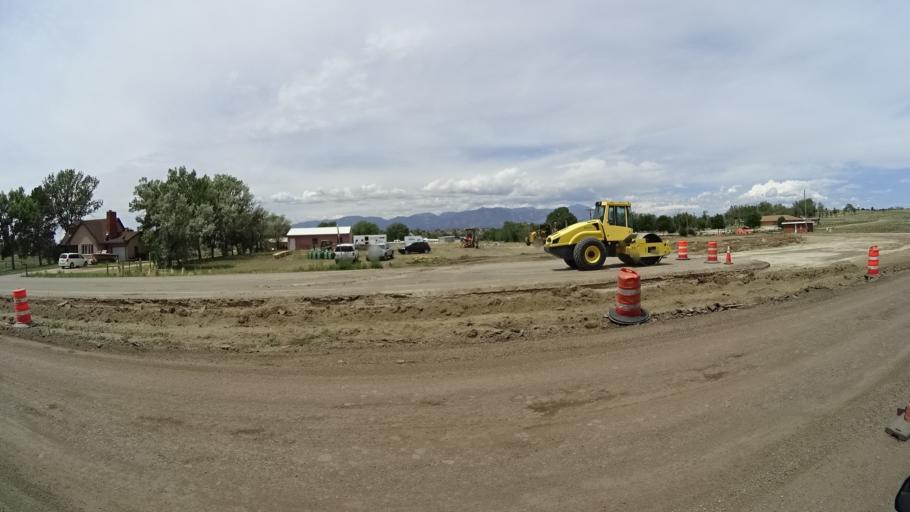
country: US
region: Colorado
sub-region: El Paso County
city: Fountain
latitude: 38.7078
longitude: -104.6734
